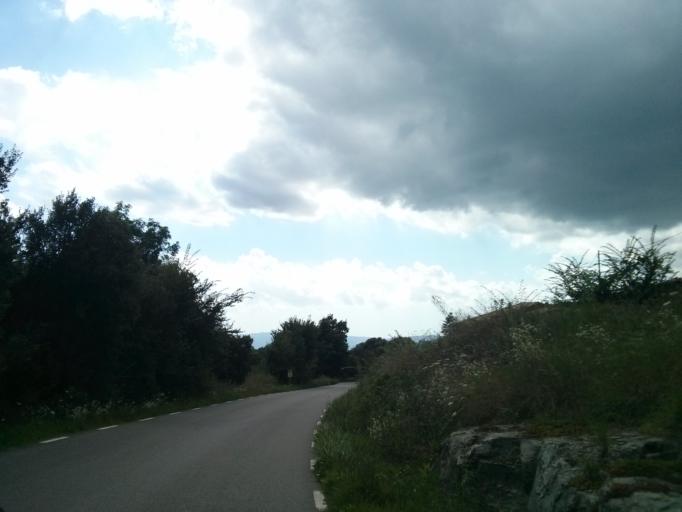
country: ES
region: Catalonia
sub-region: Provincia de Barcelona
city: Santa Maria de Corco
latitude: 42.0289
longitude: 2.3820
